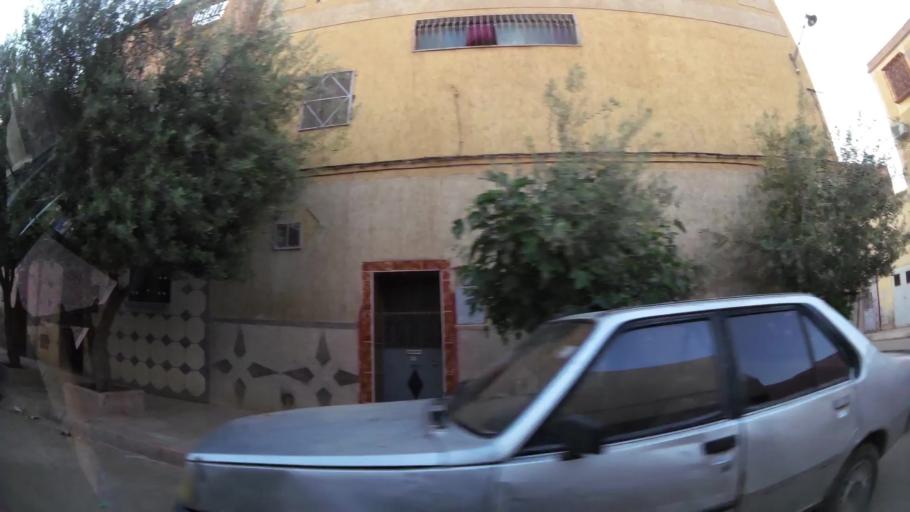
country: MA
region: Oriental
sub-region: Oujda-Angad
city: Oujda
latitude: 34.7022
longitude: -1.9112
